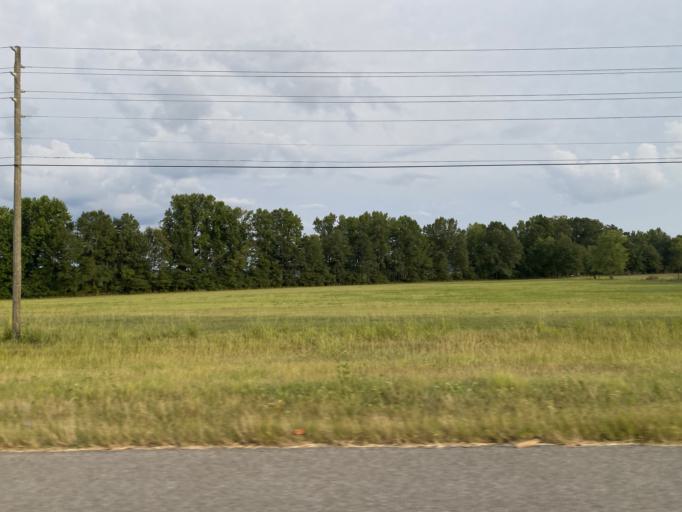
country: US
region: Alabama
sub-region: Franklin County
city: Red Bay
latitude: 34.4490
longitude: -88.0794
